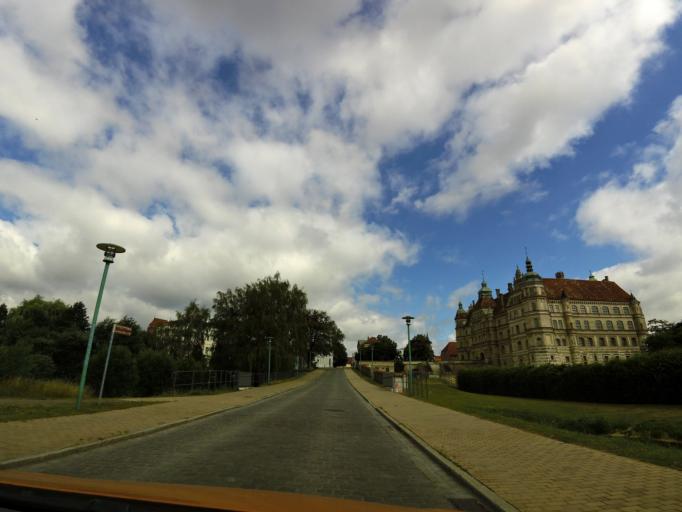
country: DE
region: Mecklenburg-Vorpommern
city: Guestrow
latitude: 53.7894
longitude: 12.1772
